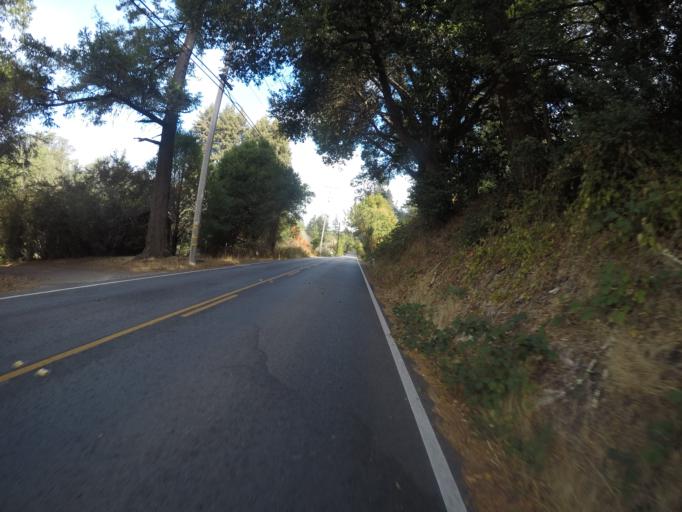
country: US
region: California
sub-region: Santa Cruz County
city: Pasatiempo
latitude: 37.0201
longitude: -121.9922
